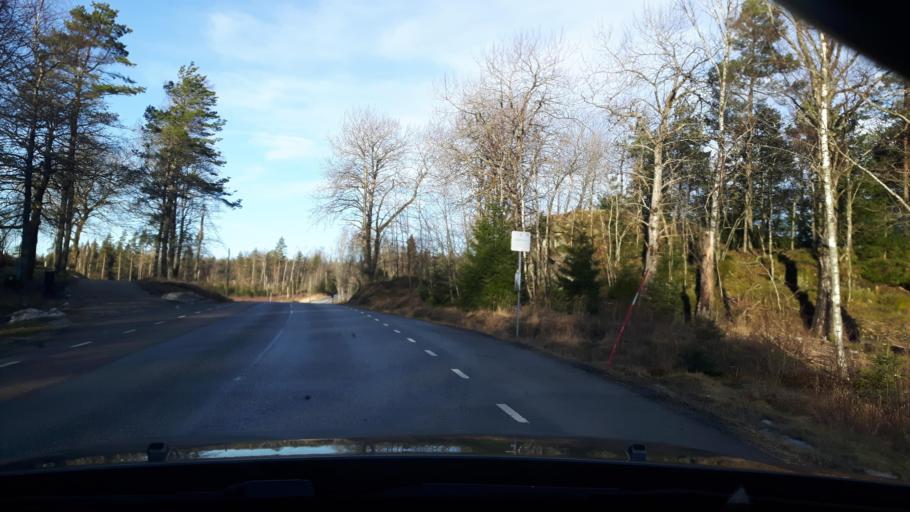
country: SE
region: Vaestra Goetaland
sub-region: Munkedals Kommun
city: Munkedal
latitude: 58.4973
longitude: 11.6925
